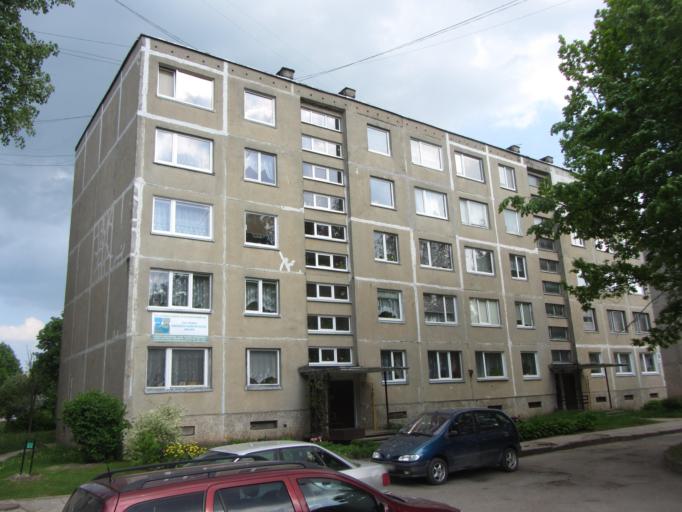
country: LT
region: Utenos apskritis
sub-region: Utena
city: Utena
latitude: 55.5095
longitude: 25.5862
